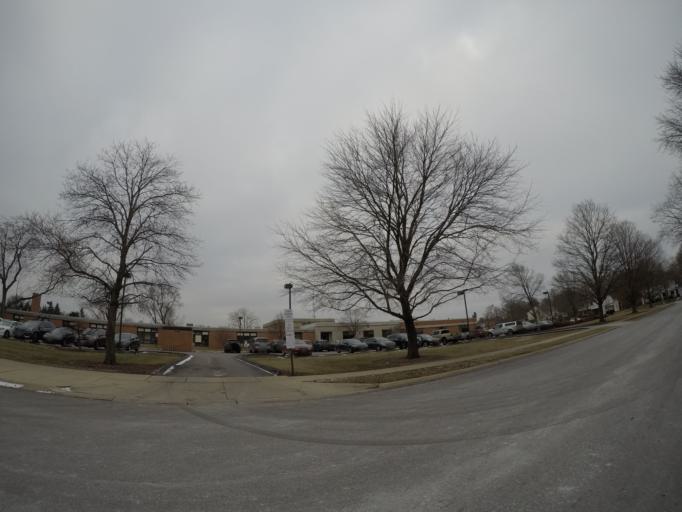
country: US
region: Ohio
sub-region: Franklin County
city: Upper Arlington
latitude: 40.0459
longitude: -83.0578
